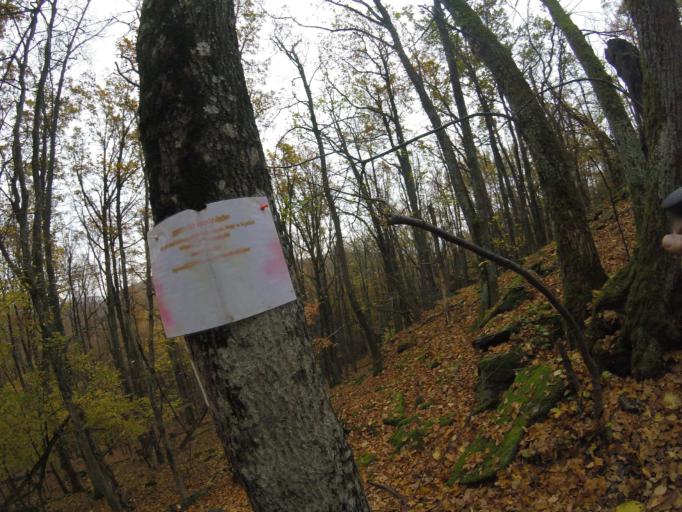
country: HU
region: Borsod-Abauj-Zemplen
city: Tolcsva
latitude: 48.3986
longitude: 21.4045
